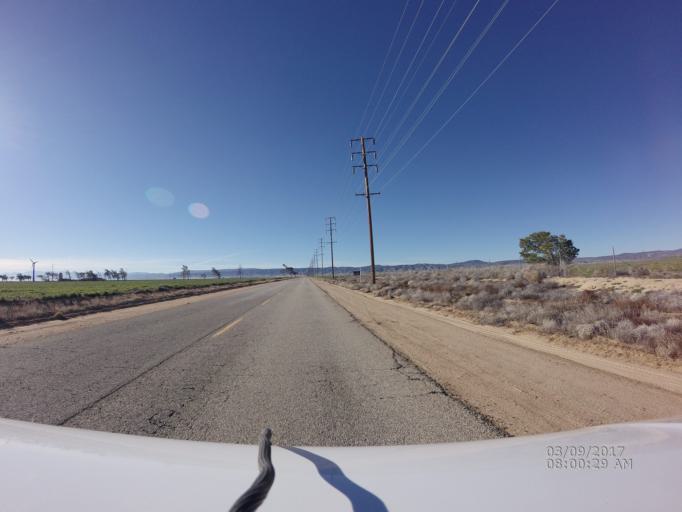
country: US
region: California
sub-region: Los Angeles County
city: Leona Valley
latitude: 34.7587
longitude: -118.3254
